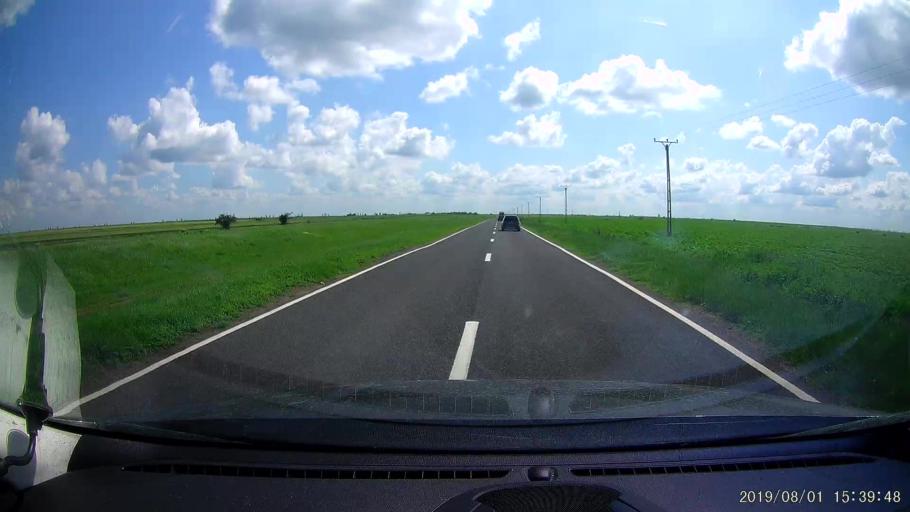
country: RO
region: Braila
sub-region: Comuna Baraganul
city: Baraganul
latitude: 44.8495
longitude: 27.5530
